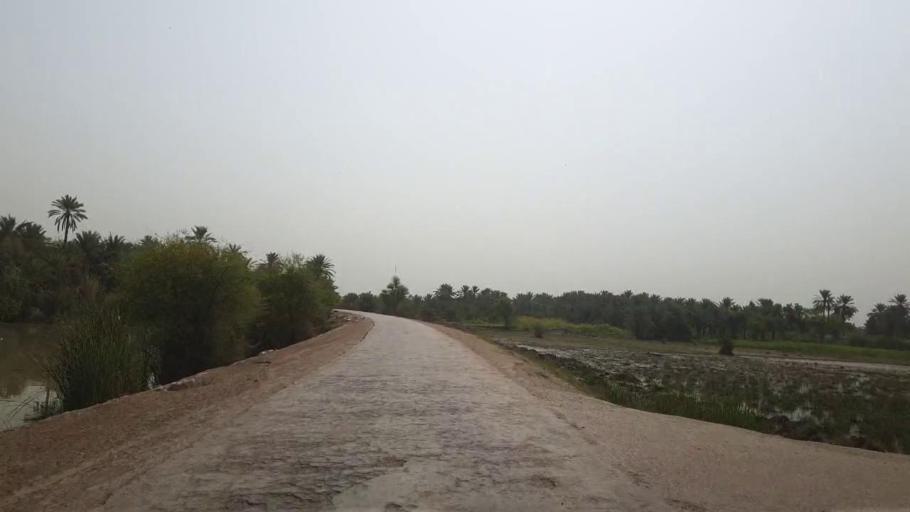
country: PK
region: Sindh
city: Gambat
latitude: 27.4310
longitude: 68.5254
